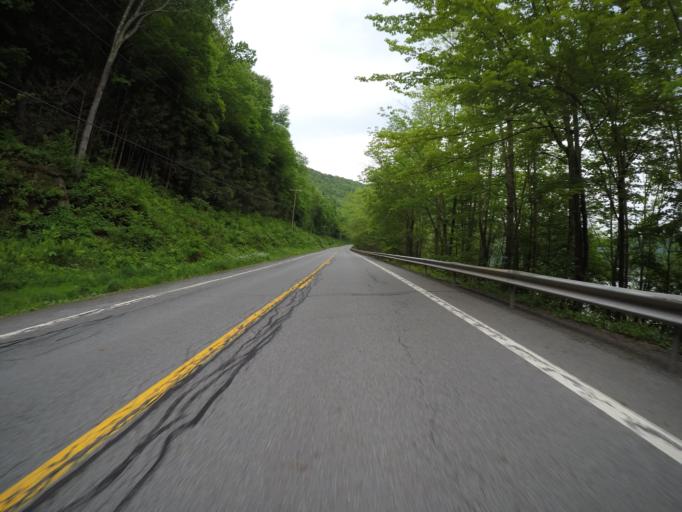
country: US
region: New York
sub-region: Sullivan County
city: Livingston Manor
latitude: 42.0733
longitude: -74.9180
